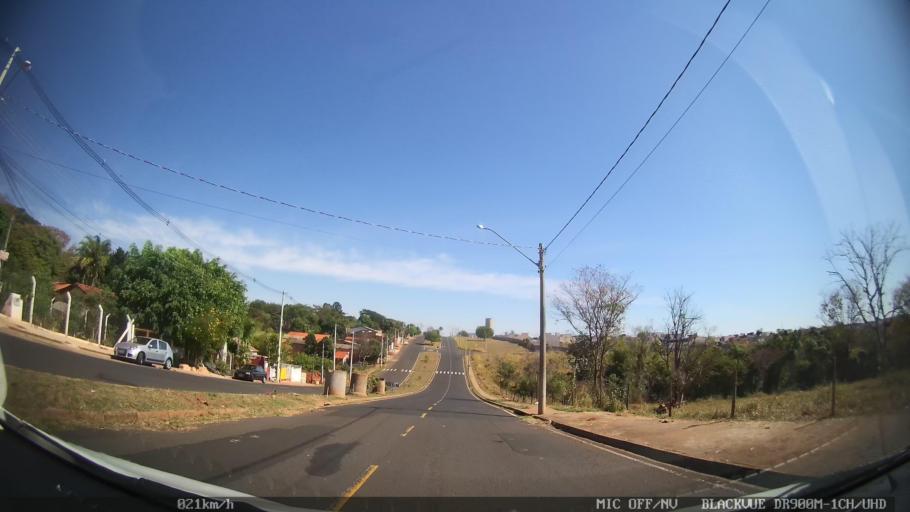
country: BR
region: Sao Paulo
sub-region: Sao Jose Do Rio Preto
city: Sao Jose do Rio Preto
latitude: -20.7667
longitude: -49.4168
